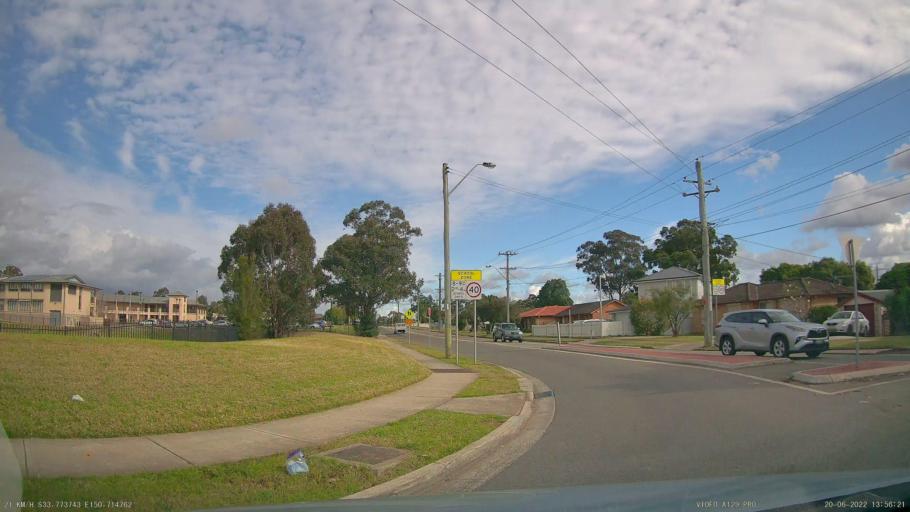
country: AU
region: New South Wales
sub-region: Penrith Municipality
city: Kingswood Park
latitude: -33.7738
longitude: 150.7147
